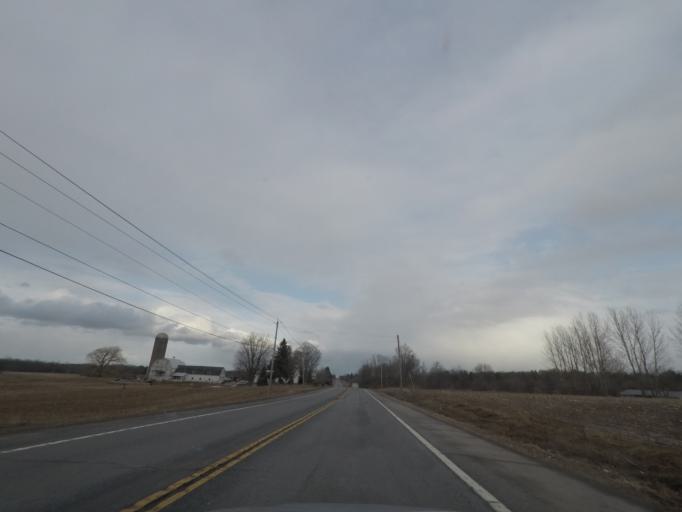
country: US
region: New York
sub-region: Oneida County
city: Vernon
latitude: 43.0722
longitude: -75.4857
